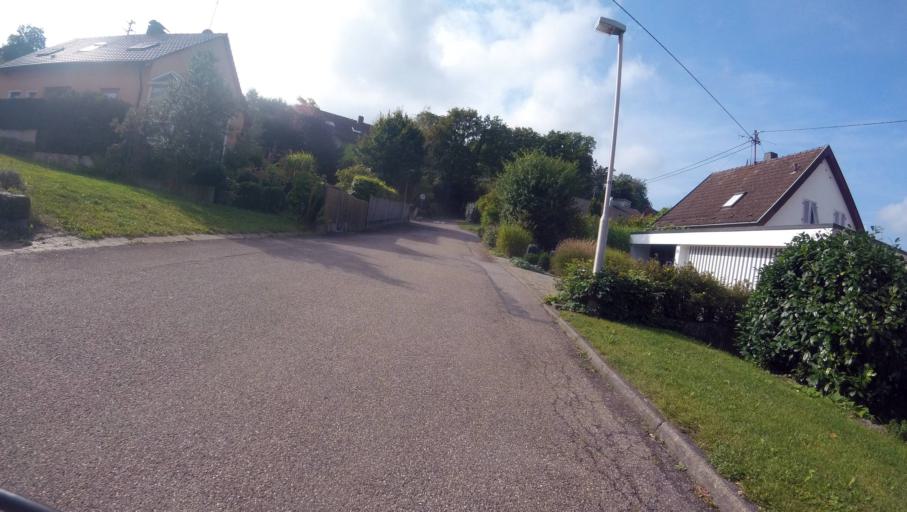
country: DE
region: Baden-Wuerttemberg
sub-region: Regierungsbezirk Stuttgart
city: Burgstetten
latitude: 48.9268
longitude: 9.3702
